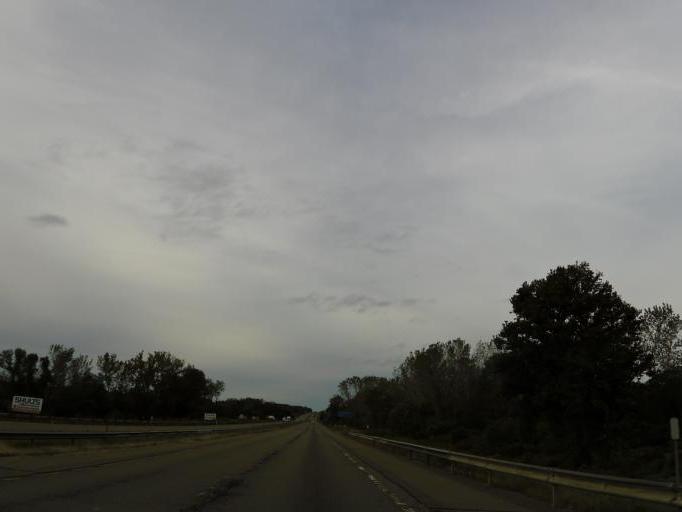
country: US
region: New York
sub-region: Erie County
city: Lake Erie Beach
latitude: 42.5609
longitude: -79.0967
